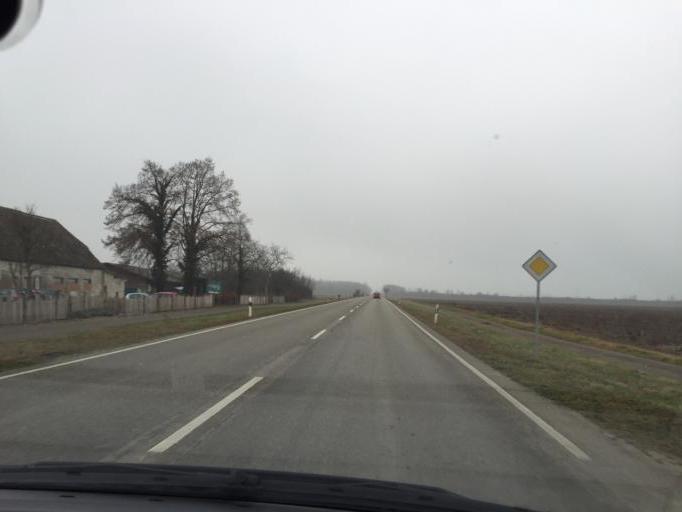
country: DE
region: Baden-Wuerttemberg
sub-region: Freiburg Region
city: Ihringen
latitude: 47.9981
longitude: 7.6282
